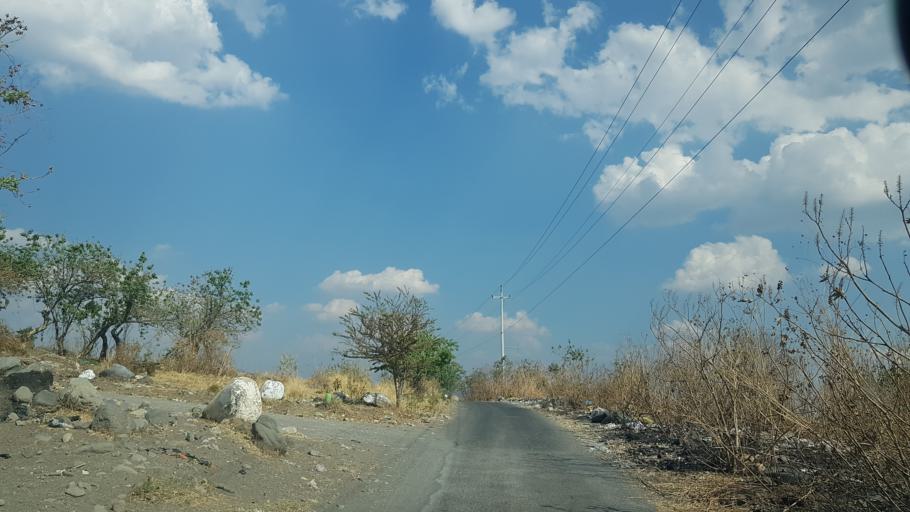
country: MX
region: Puebla
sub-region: Atlixco
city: Colonia Agricola de Ocotepec (Colonia San Jose)
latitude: 18.8890
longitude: -98.5024
